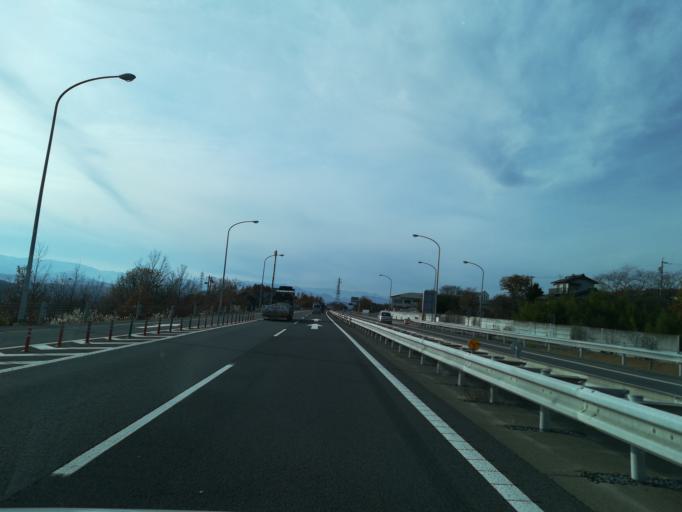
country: JP
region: Nagano
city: Komoro
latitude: 36.3456
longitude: 138.4064
